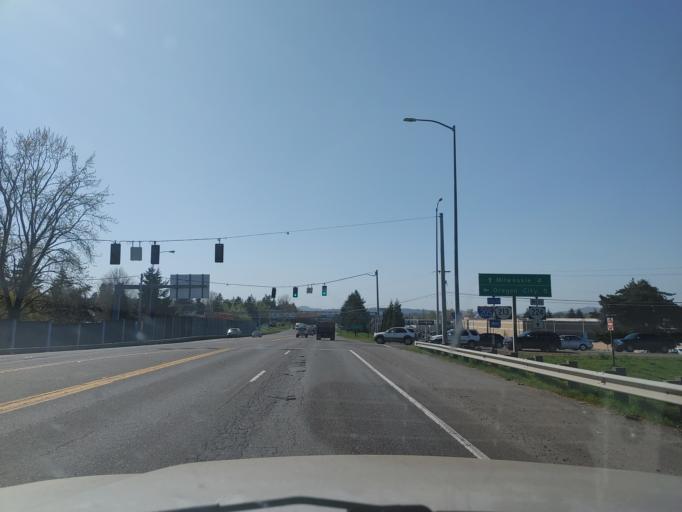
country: US
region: Oregon
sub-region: Clackamas County
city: Clackamas
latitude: 45.4217
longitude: -122.5774
